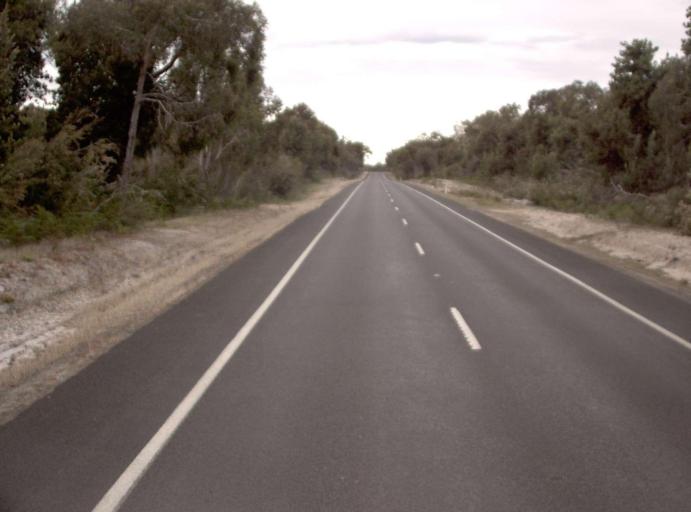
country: AU
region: Victoria
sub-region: Wellington
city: Sale
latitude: -38.3380
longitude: 147.0096
